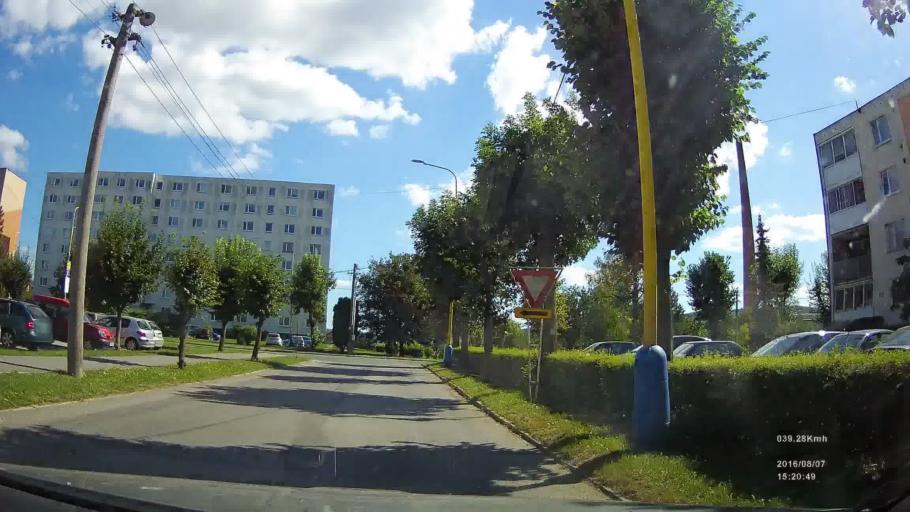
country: SK
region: Presovsky
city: Stropkov
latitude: 49.1997
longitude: 21.6485
